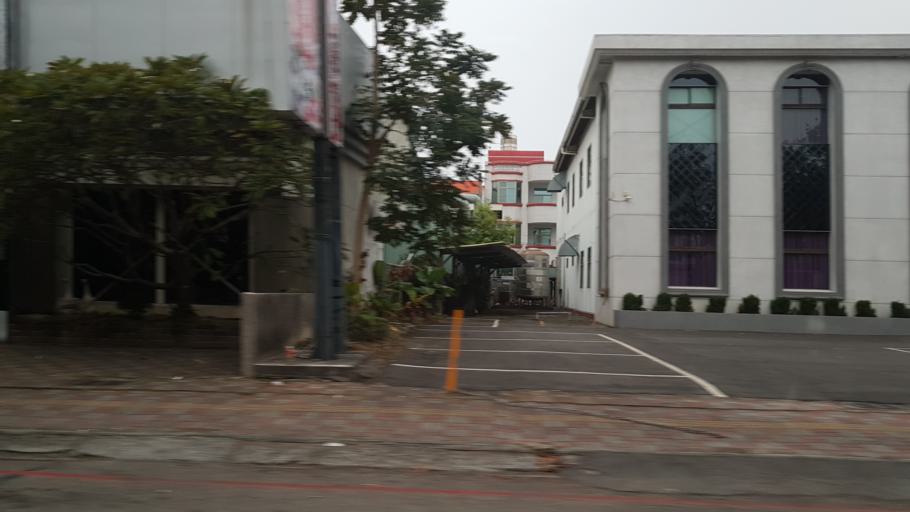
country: TW
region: Taiwan
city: Xinying
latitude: 23.3121
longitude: 120.3122
